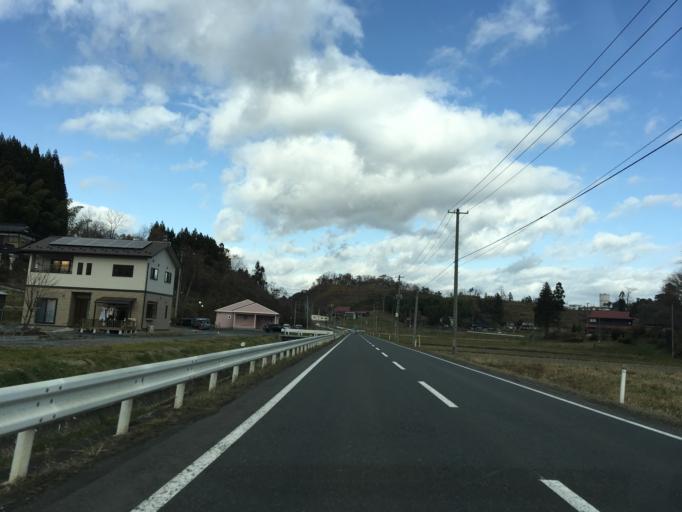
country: JP
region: Iwate
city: Ichinoseki
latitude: 38.8962
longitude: 141.1594
